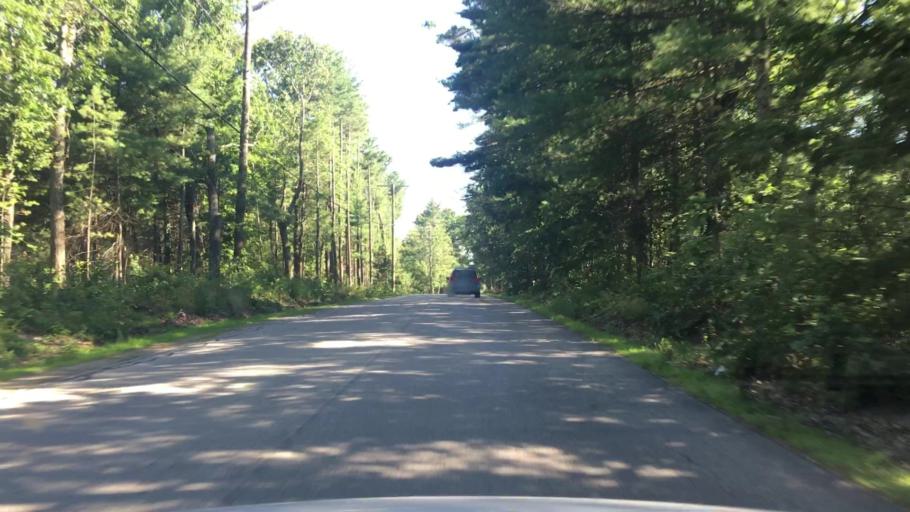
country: US
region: New Hampshire
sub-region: Rockingham County
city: Brentwood
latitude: 42.9980
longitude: -71.0147
